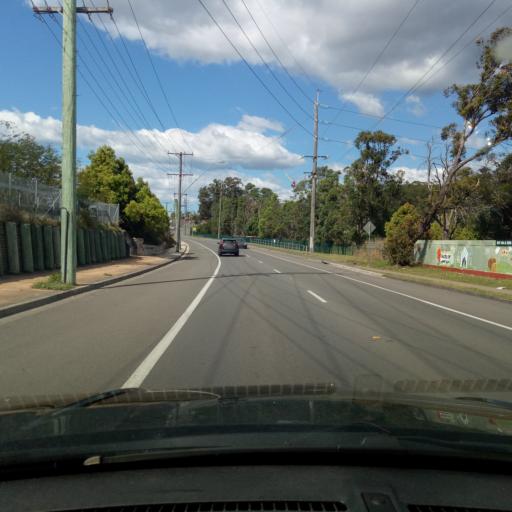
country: AU
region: New South Wales
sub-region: Gosford Shire
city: Gosford
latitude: -33.4153
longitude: 151.3423
